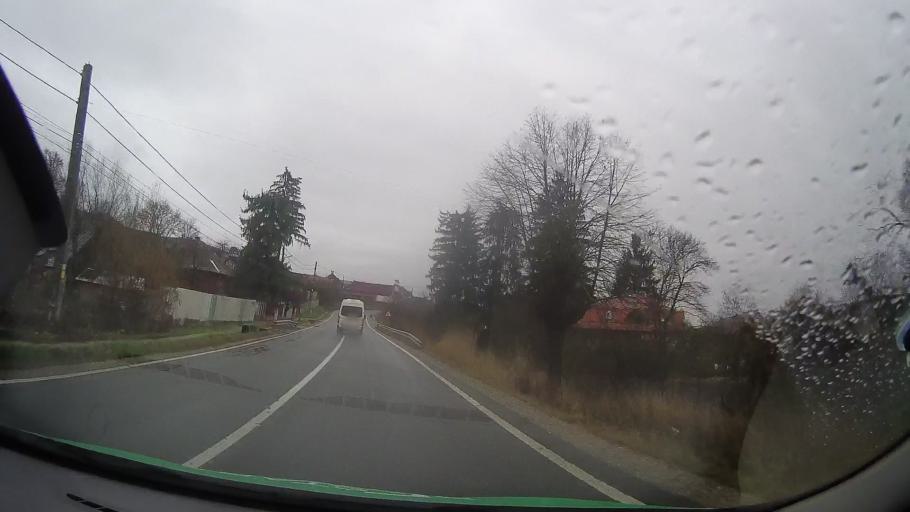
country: RO
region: Bistrita-Nasaud
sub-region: Comuna Galatii Bistritei
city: Galatii Bistritei
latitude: 47.0217
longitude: 24.4152
